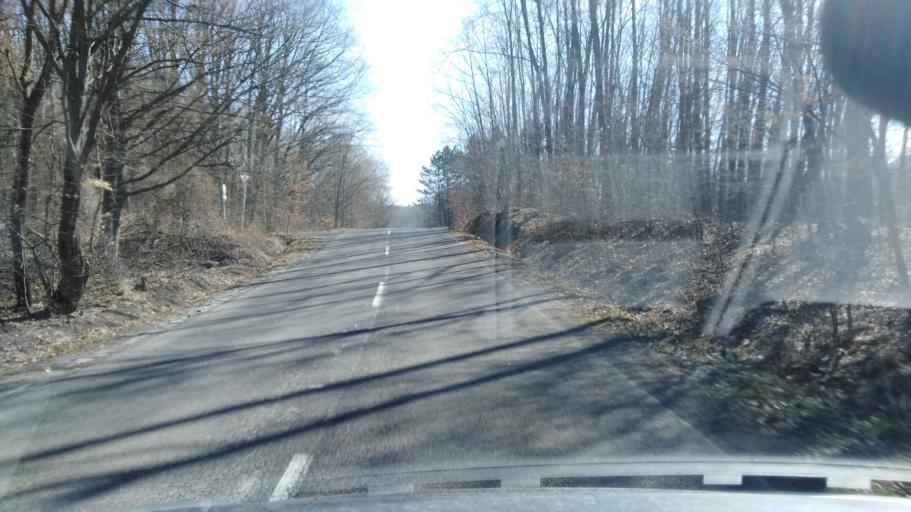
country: HU
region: Nograd
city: Somoskoujfalu
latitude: 48.1534
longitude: 19.8568
